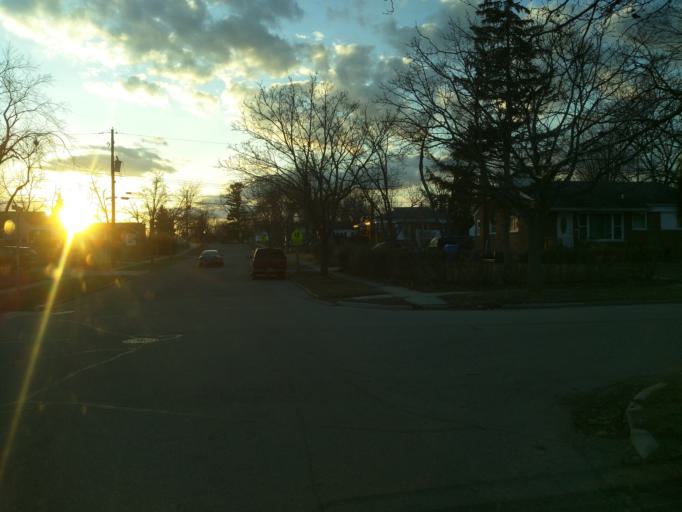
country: US
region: Michigan
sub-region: Ingham County
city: Edgemont Park
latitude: 42.7582
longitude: -84.5855
